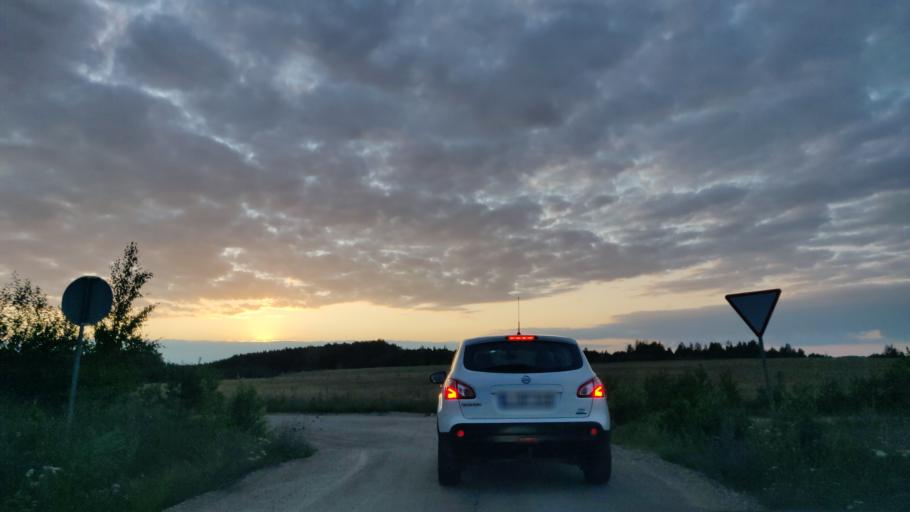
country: LT
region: Vilnius County
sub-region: Trakai
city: Rudiskes
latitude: 54.6067
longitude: 24.7827
